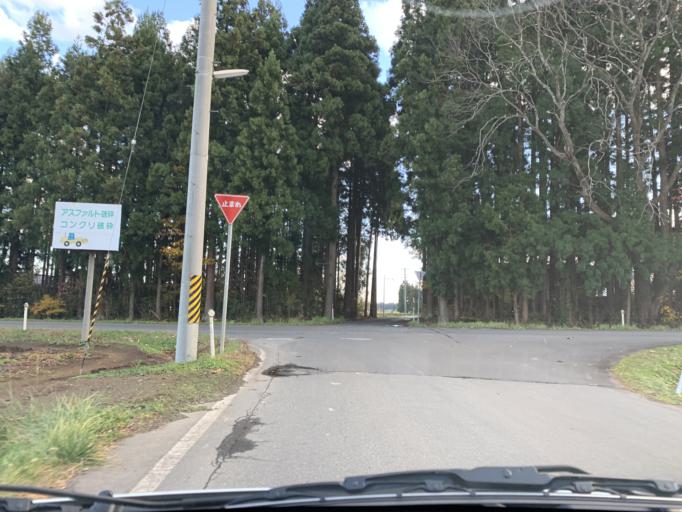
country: JP
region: Iwate
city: Mizusawa
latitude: 39.1158
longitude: 141.0382
